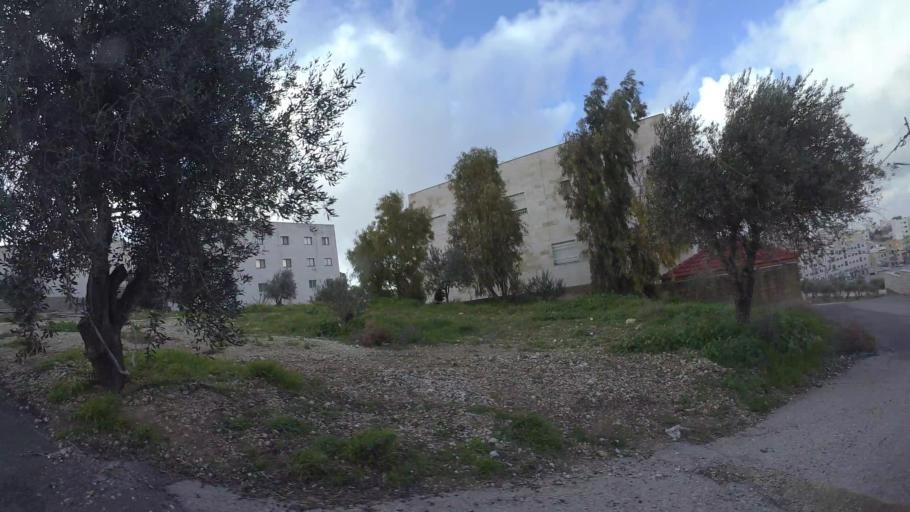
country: JO
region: Amman
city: Al Jubayhah
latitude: 32.0530
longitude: 35.8878
